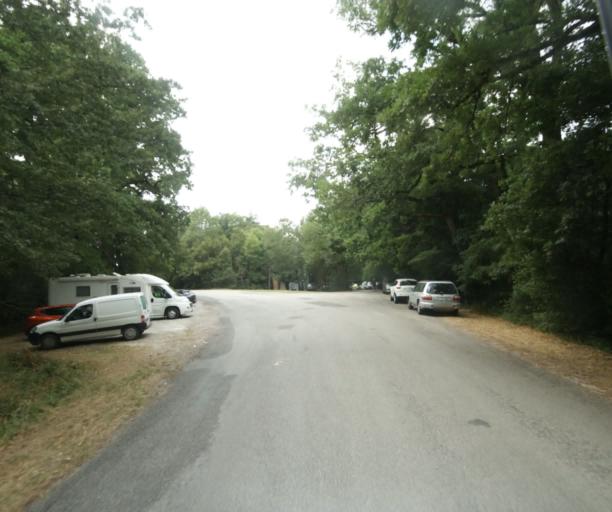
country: FR
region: Midi-Pyrenees
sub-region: Departement de la Haute-Garonne
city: Revel
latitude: 43.4321
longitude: 2.0265
